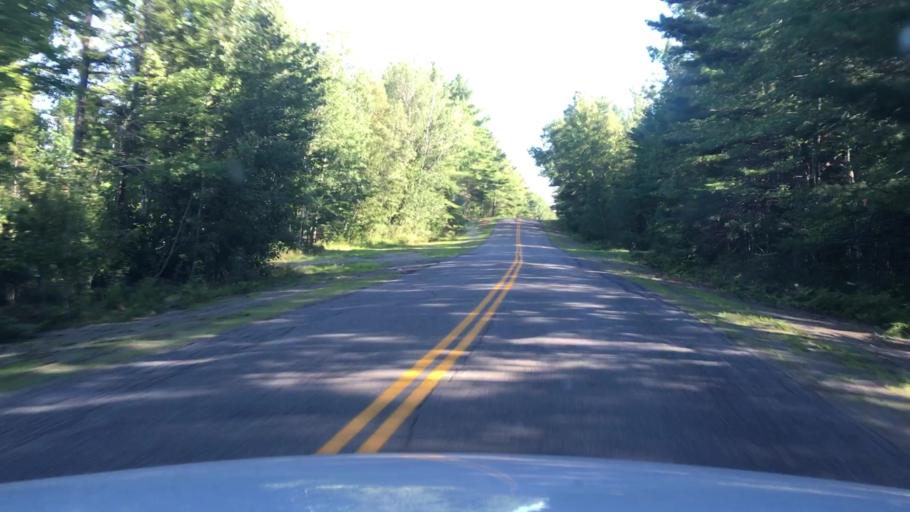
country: US
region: Maine
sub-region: Penobscot County
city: Enfield
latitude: 45.2310
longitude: -68.5806
